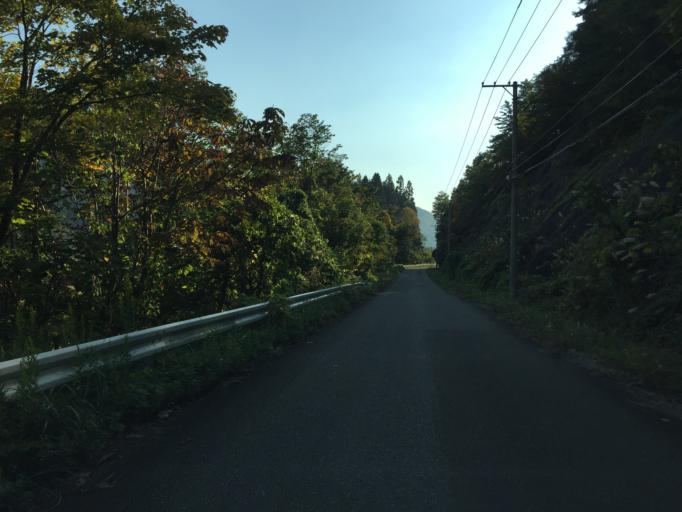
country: JP
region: Fukushima
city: Kitakata
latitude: 37.7510
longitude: 139.9013
